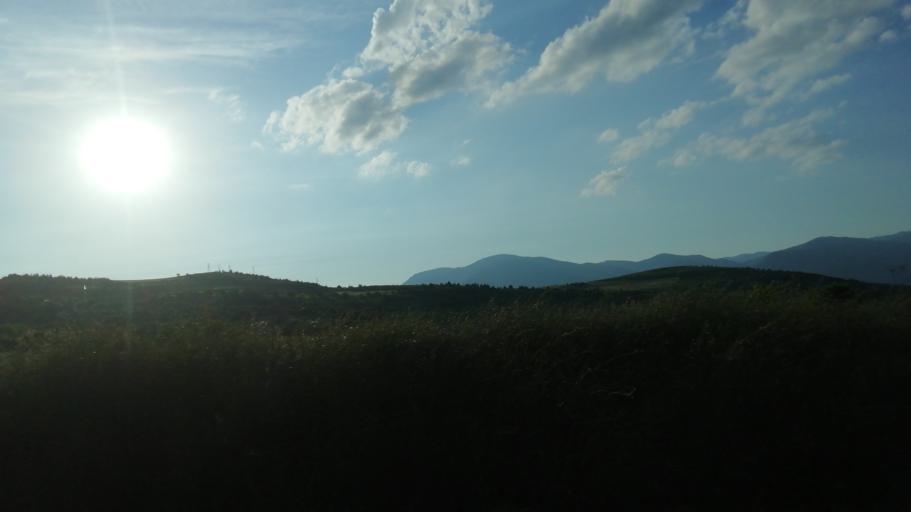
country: TR
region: Karabuk
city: Karabuk
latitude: 41.1320
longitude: 32.6255
